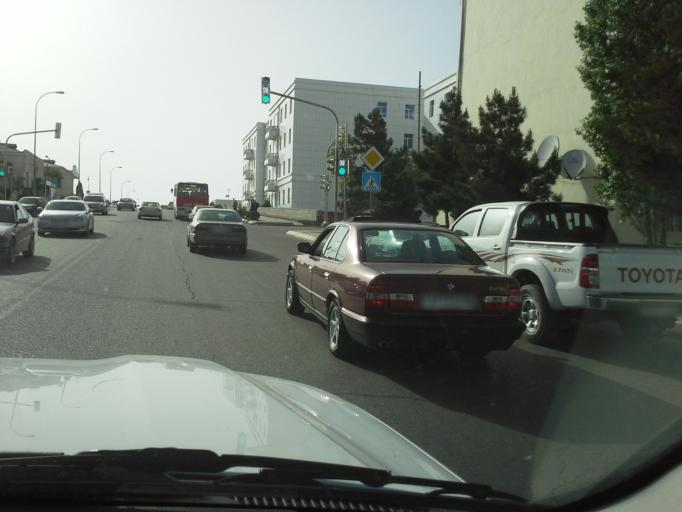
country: TM
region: Balkan
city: Turkmenbasy
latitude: 40.0168
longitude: 52.9773
